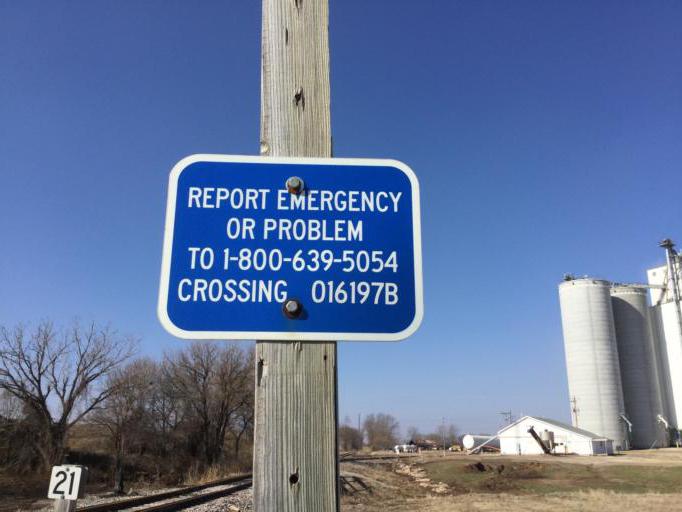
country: US
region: Kansas
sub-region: Barber County
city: Medicine Lodge
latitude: 37.2840
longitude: -98.5937
